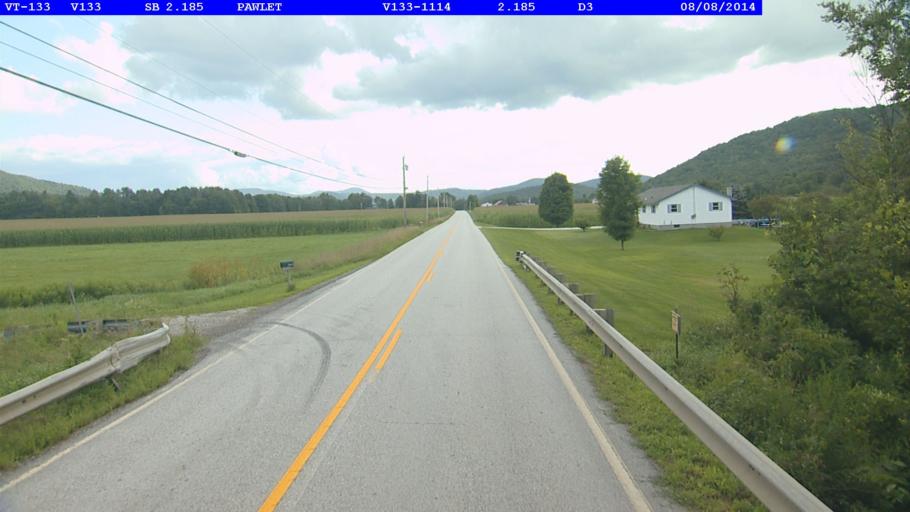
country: US
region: New York
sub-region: Washington County
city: Granville
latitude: 43.3636
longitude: -73.1484
